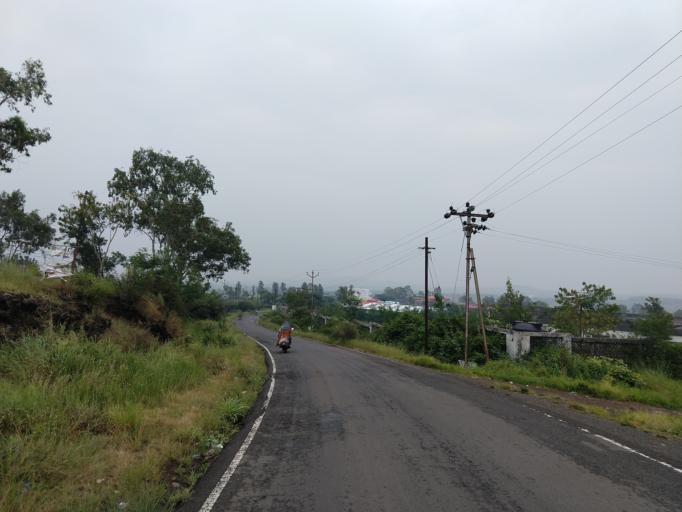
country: IN
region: Maharashtra
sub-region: Pune Division
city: Khed
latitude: 18.4046
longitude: 73.9105
